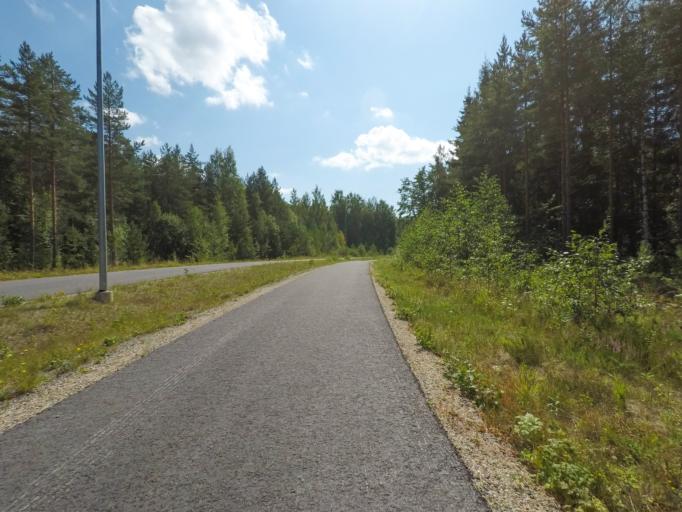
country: FI
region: Southern Savonia
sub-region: Mikkeli
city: Puumala
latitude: 61.5090
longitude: 28.1689
